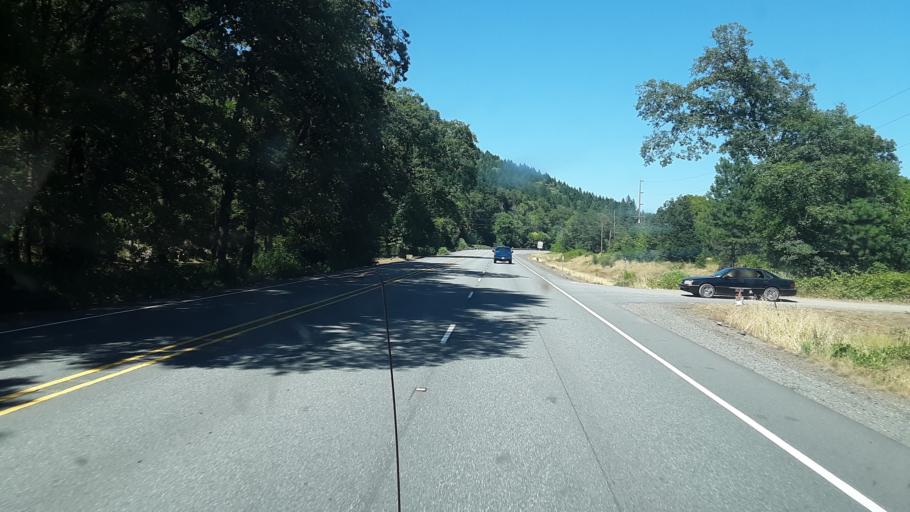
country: US
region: Oregon
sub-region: Josephine County
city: Redwood
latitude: 42.3672
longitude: -123.5079
